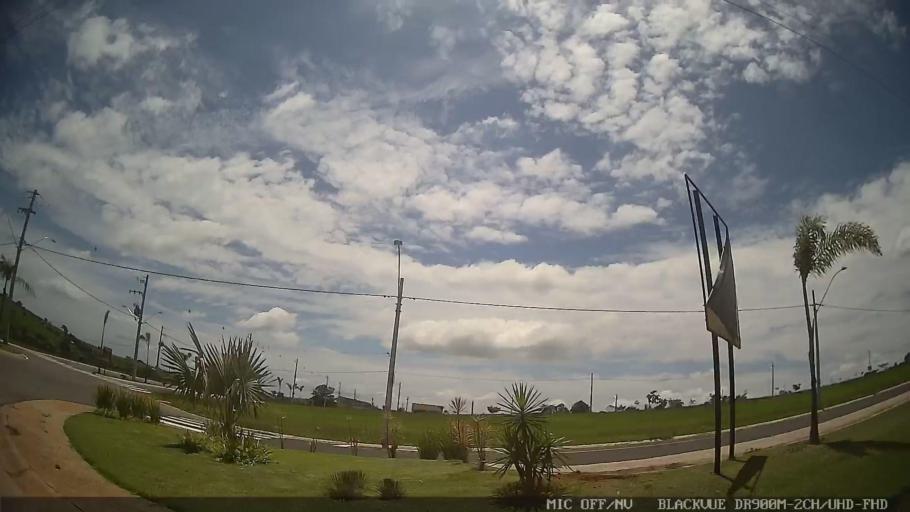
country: BR
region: Sao Paulo
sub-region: Laranjal Paulista
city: Laranjal Paulista
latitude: -23.0303
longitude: -47.8387
